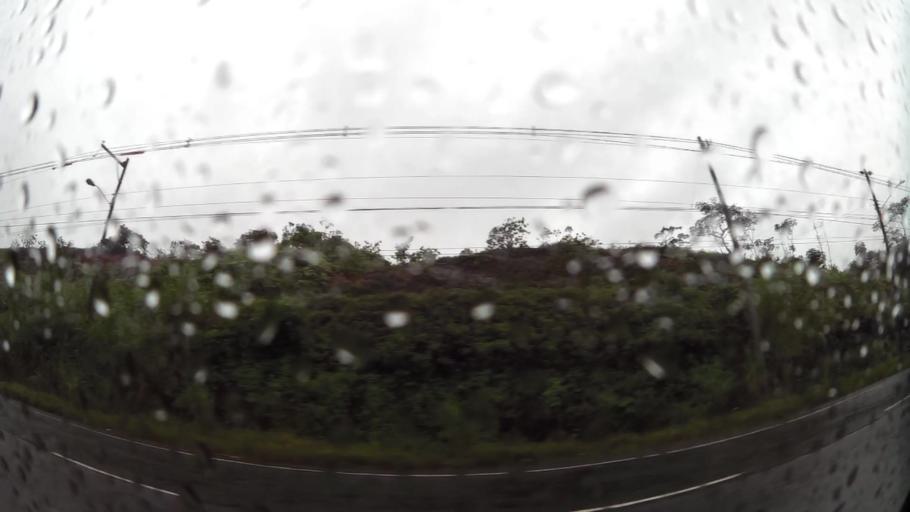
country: PA
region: Colon
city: Gatun
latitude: 9.2887
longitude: -79.7539
